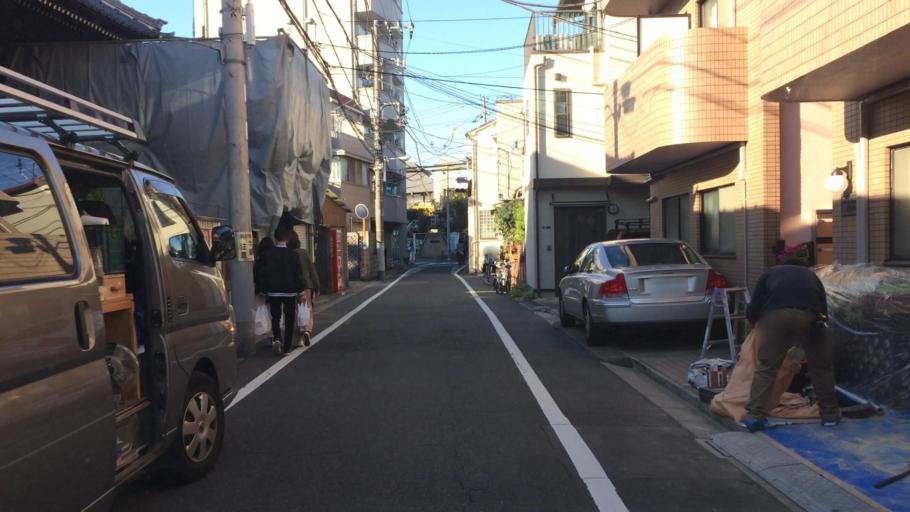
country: JP
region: Tokyo
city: Tokyo
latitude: 35.7230
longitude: 139.7686
